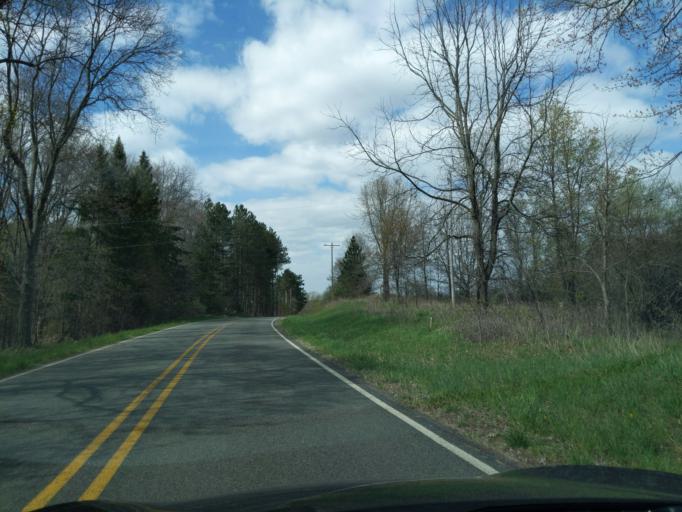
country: US
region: Michigan
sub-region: Ingham County
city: Leslie
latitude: 42.4199
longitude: -84.5414
